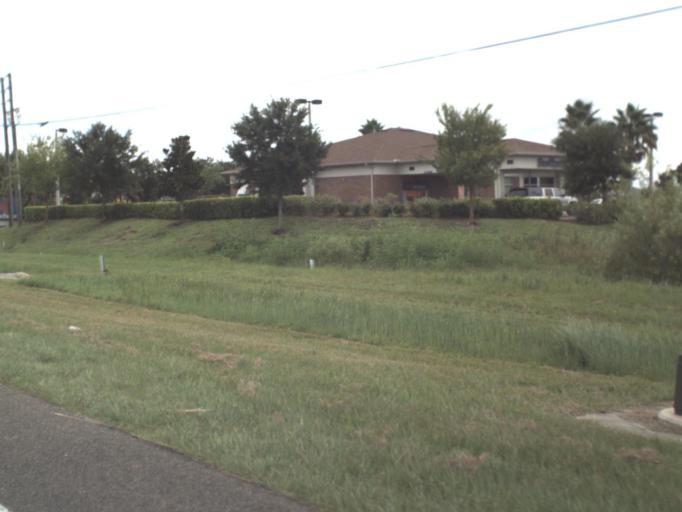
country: US
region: Florida
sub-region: Pasco County
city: Odessa
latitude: 28.1871
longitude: -82.5497
